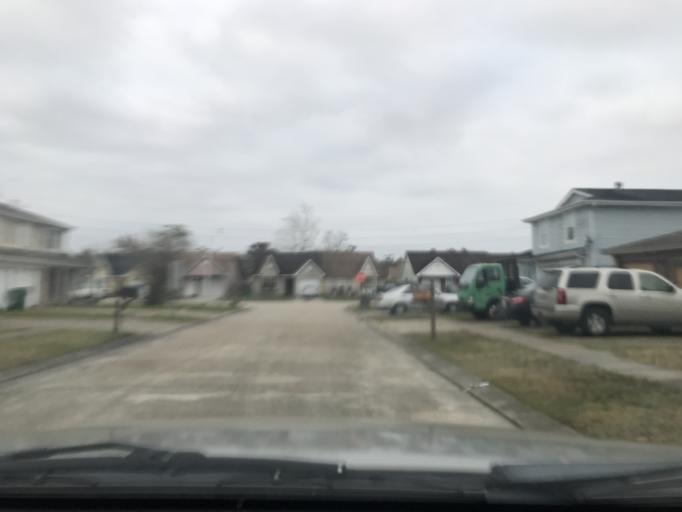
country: US
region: Louisiana
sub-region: Jefferson Parish
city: Woodmere
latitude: 29.8594
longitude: -90.0748
